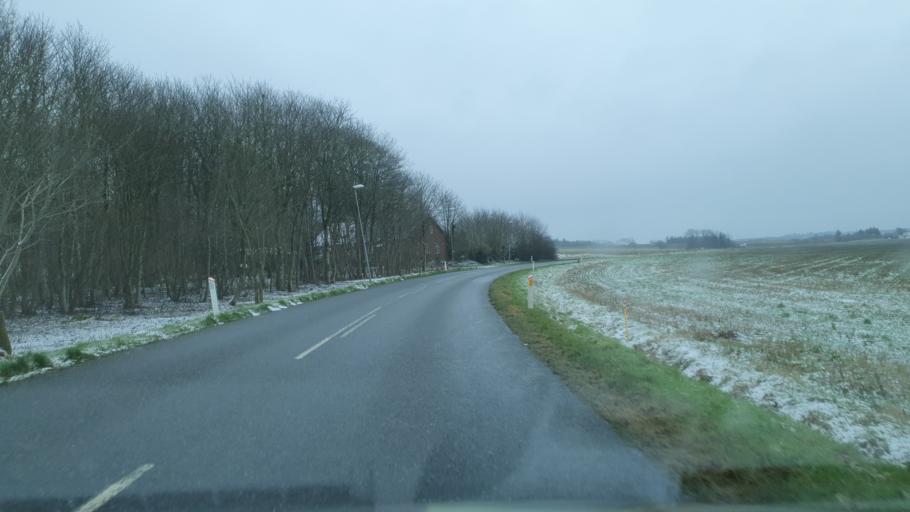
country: DK
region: North Denmark
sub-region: Jammerbugt Kommune
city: Brovst
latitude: 57.1318
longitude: 9.4699
